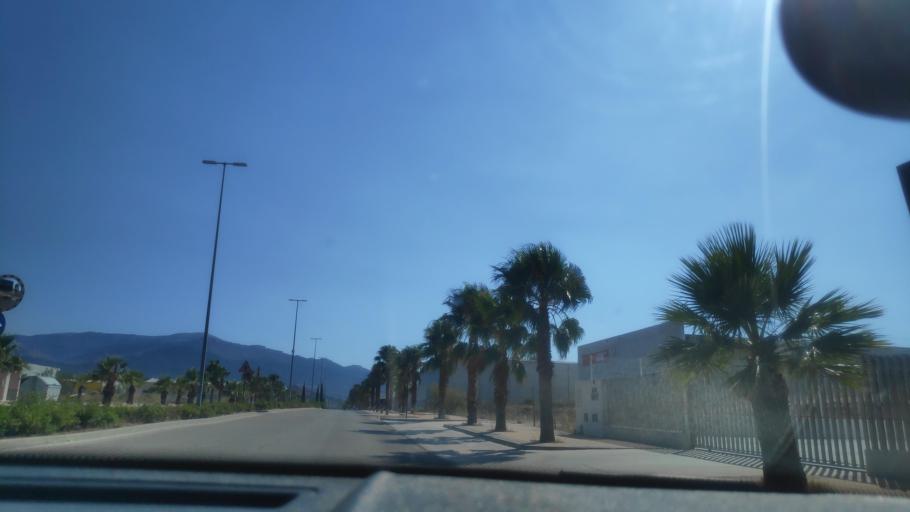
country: ES
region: Andalusia
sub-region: Provincia de Jaen
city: Jaen
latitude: 37.8175
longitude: -3.7810
